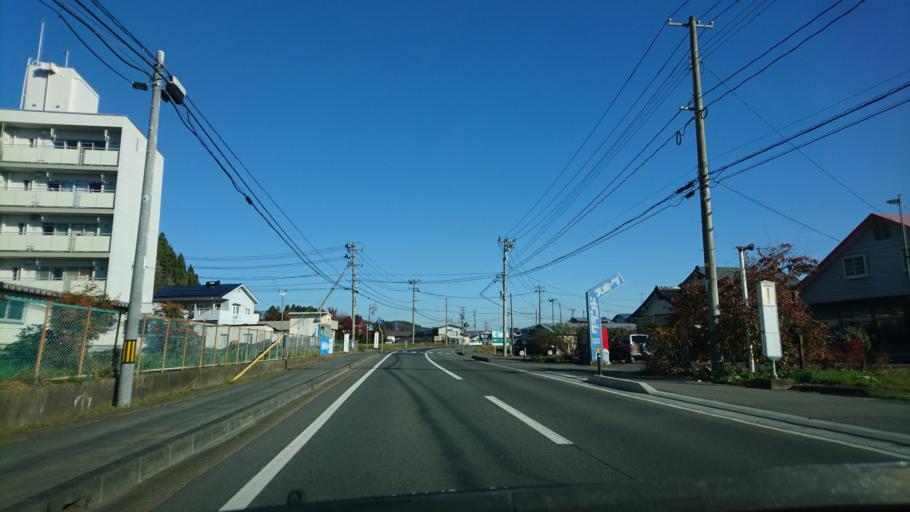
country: JP
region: Iwate
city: Mizusawa
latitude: 39.0635
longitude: 141.1258
